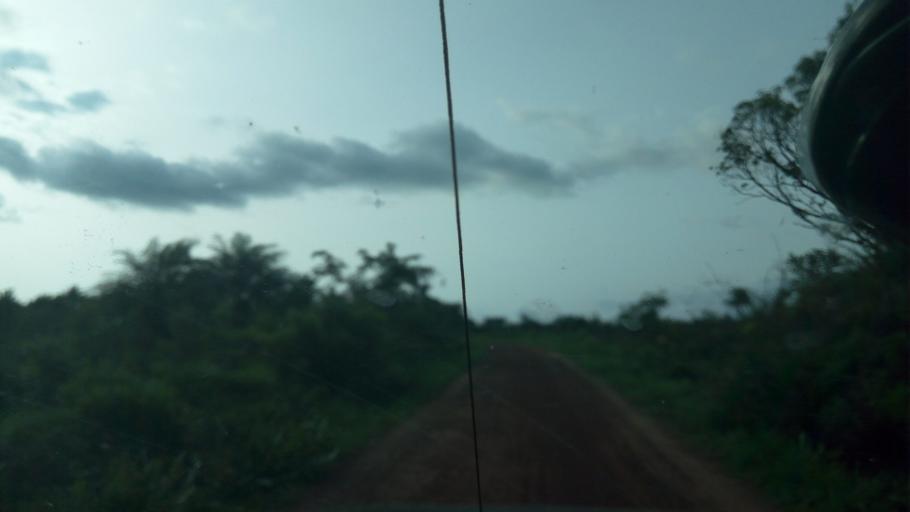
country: SL
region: Northern Province
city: Mambolo
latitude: 8.9927
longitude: -13.0071
